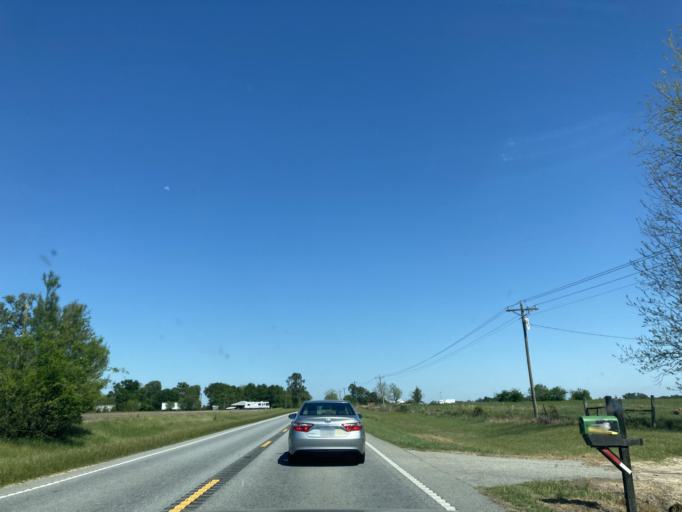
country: US
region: Georgia
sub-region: Miller County
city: Colquitt
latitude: 31.1865
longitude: -84.6387
